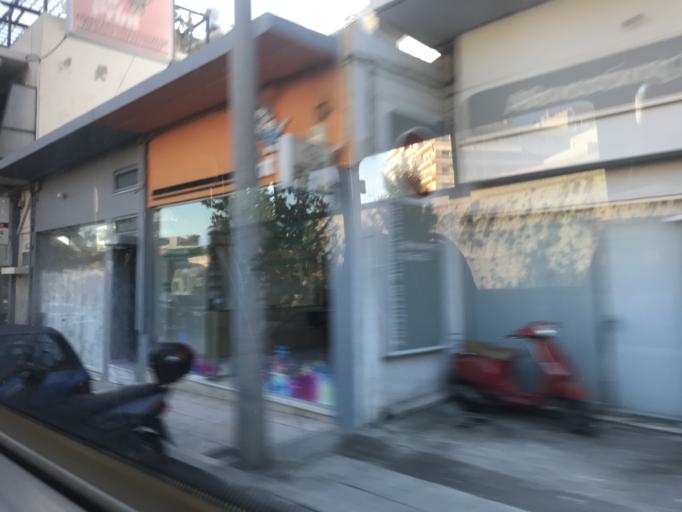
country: GR
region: Crete
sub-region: Nomos Irakleiou
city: Irakleion
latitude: 35.3384
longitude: 25.1384
